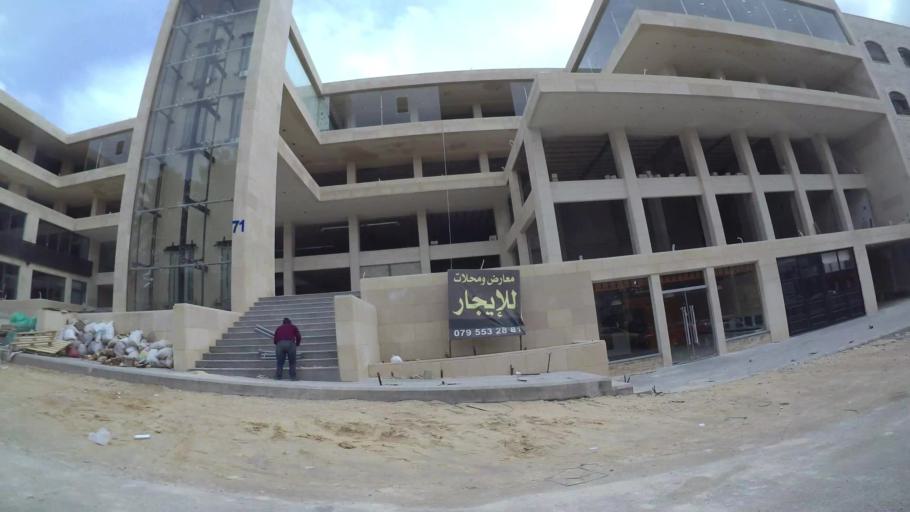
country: JO
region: Amman
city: Umm as Summaq
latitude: 31.8915
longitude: 35.8603
